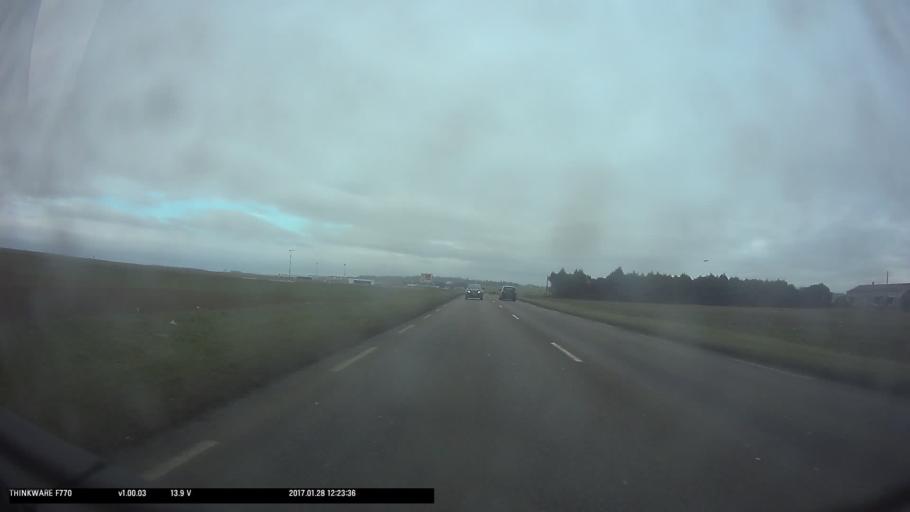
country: FR
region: Ile-de-France
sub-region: Departement du Val-d'Oise
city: Osny
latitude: 49.0956
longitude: 2.0507
